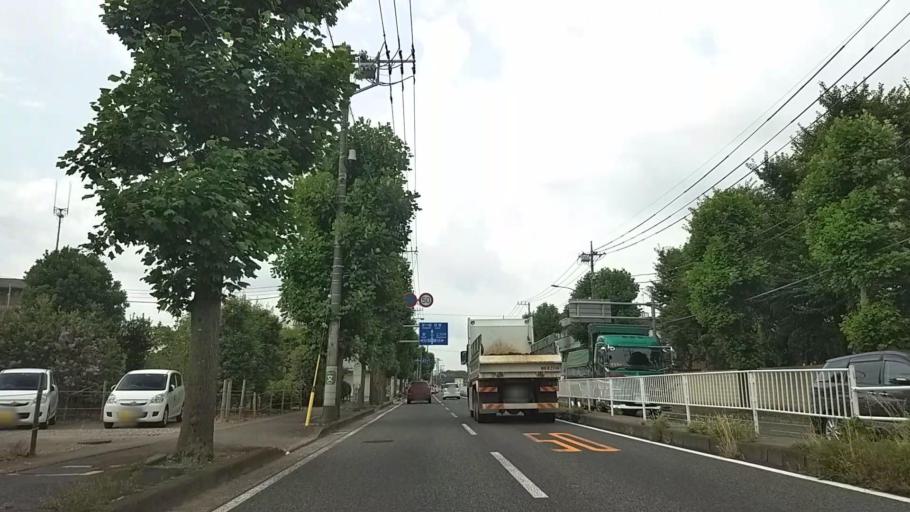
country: JP
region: Kanagawa
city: Minami-rinkan
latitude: 35.4601
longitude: 139.4829
